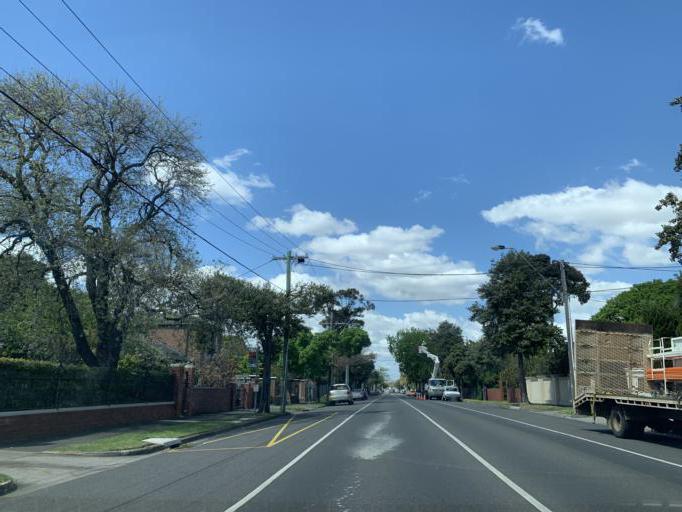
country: AU
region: Victoria
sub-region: Bayside
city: North Brighton
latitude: -37.9039
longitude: 144.9894
